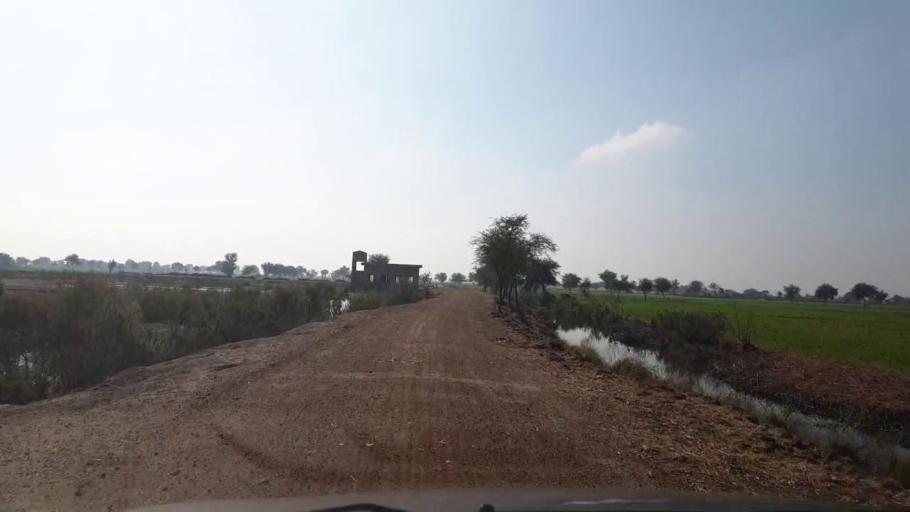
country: PK
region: Sindh
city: Sinjhoro
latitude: 26.0506
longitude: 68.7833
